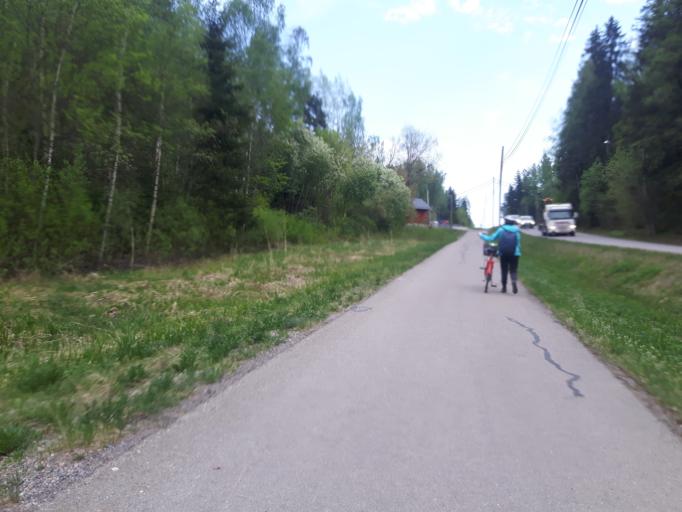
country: FI
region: Uusimaa
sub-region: Porvoo
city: Porvoo
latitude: 60.3986
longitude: 25.7302
